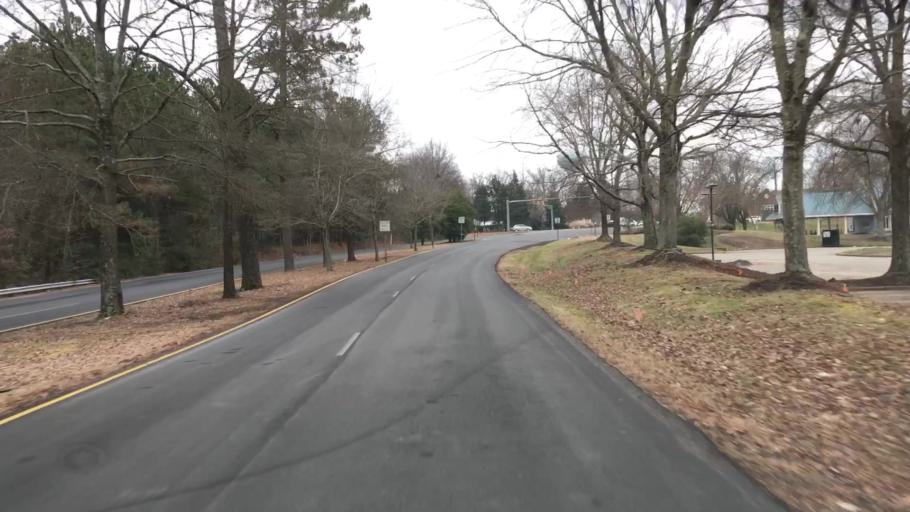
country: US
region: Virginia
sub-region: Chesterfield County
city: Bon Air
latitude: 37.5391
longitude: -77.5634
